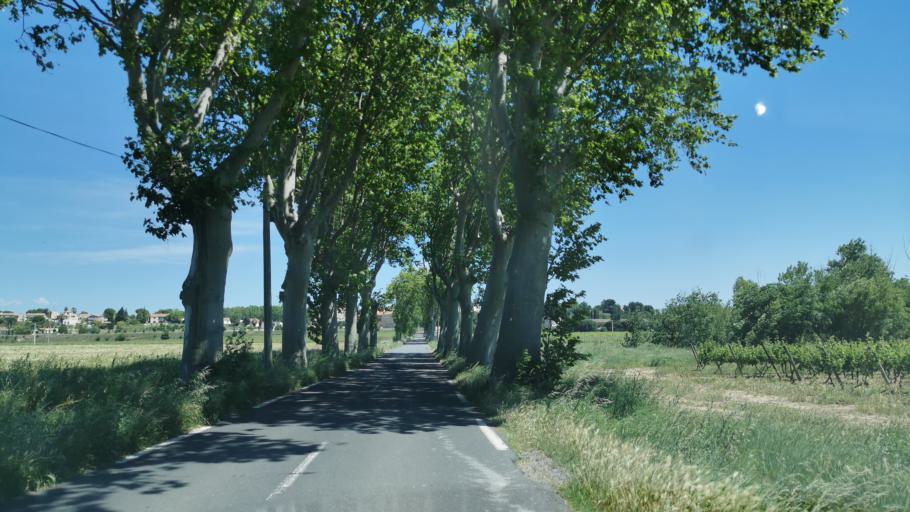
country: FR
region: Languedoc-Roussillon
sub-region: Departement de l'Aude
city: Canet
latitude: 43.2427
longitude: 2.8551
